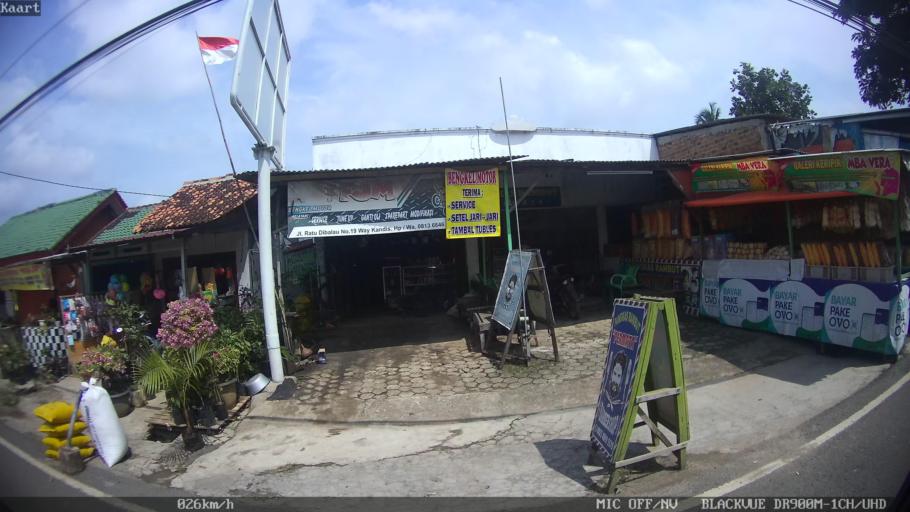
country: ID
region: Lampung
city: Kedaton
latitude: -5.3532
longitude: 105.2905
